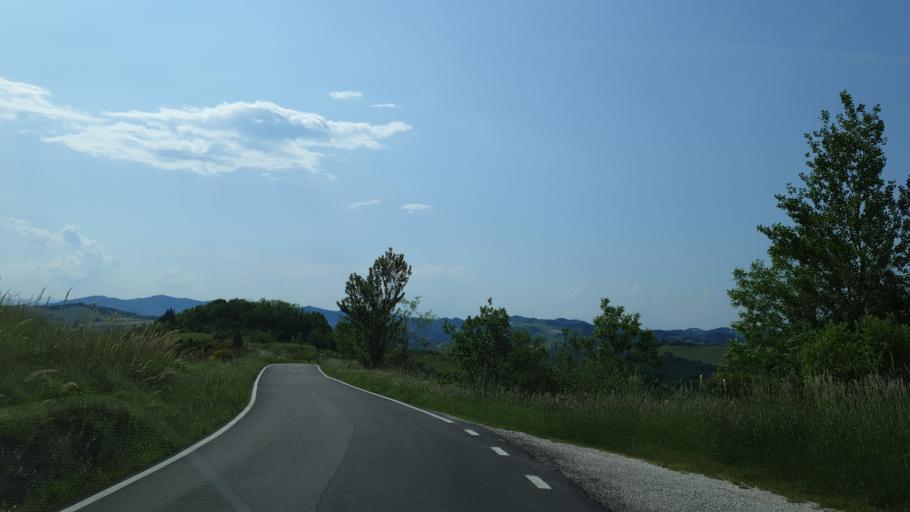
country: IT
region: Emilia-Romagna
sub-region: Provincia di Rimini
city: Sant'Agata Feltria
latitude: 43.9085
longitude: 12.2184
